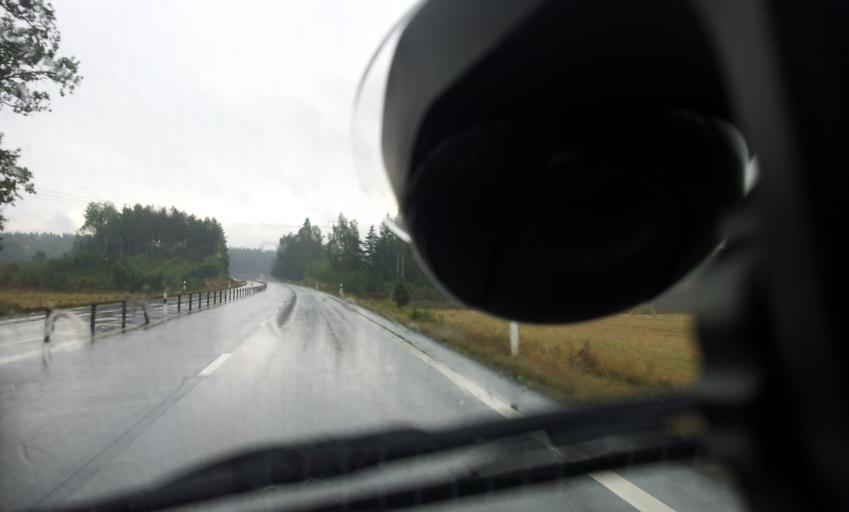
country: SE
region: Kalmar
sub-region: Vasterviks Kommun
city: Forserum
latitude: 58.0739
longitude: 16.5183
